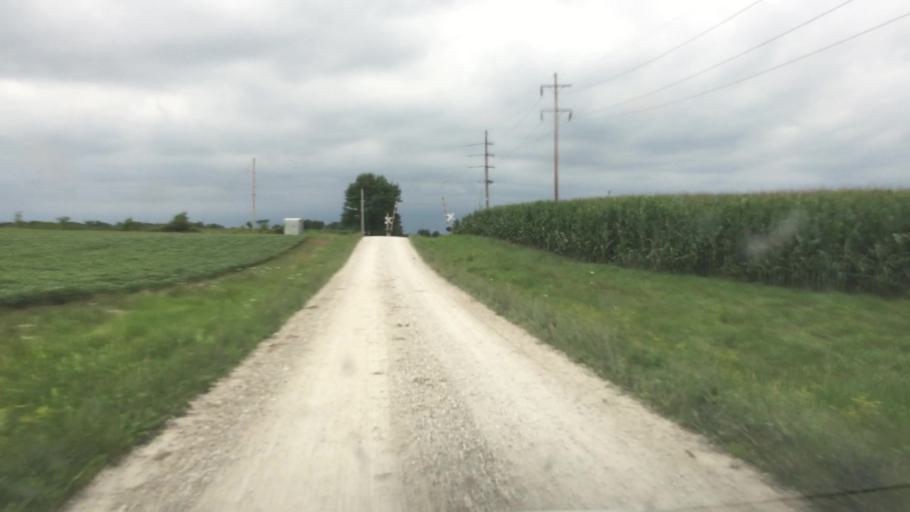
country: US
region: Illinois
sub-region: Adams County
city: Camp Point
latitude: 40.2155
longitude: -90.9583
